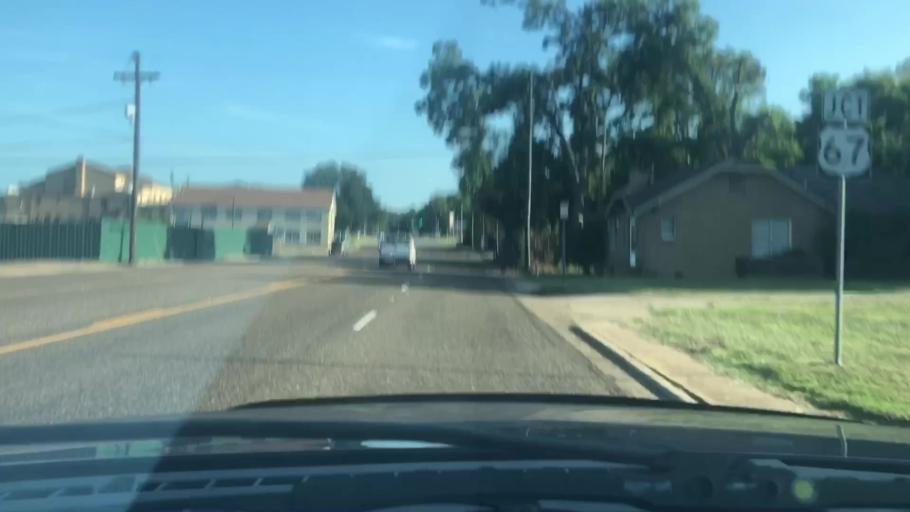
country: US
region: Texas
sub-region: Bowie County
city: Texarkana
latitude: 33.4205
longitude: -94.0610
